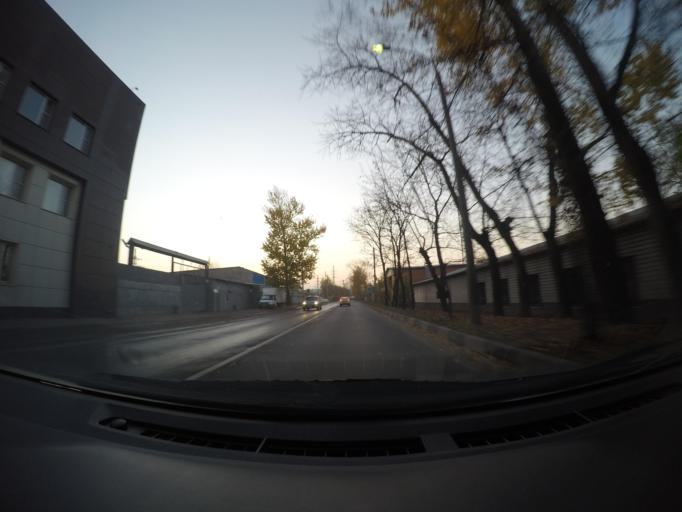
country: RU
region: Moskovskaya
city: Lyubertsy
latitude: 55.6666
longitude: 37.8892
